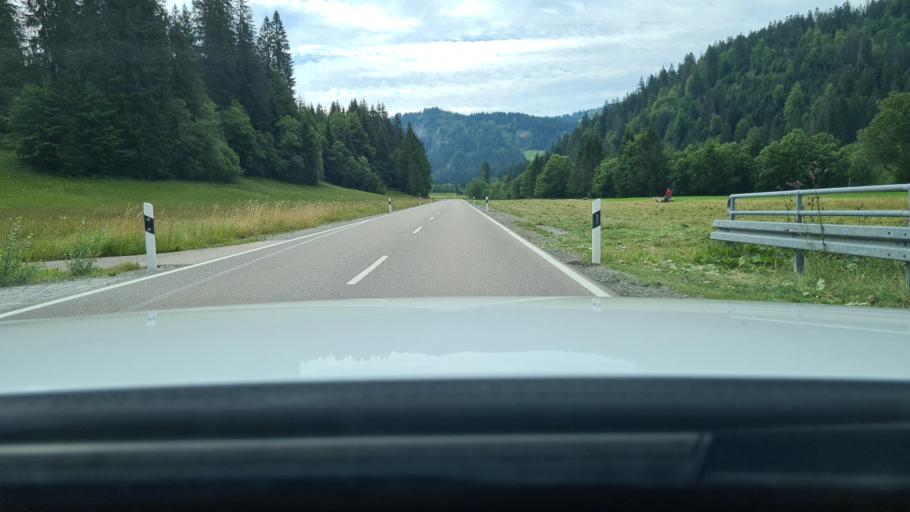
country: DE
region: Bavaria
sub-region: Swabia
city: Balderschwang
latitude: 47.4517
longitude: 10.1330
